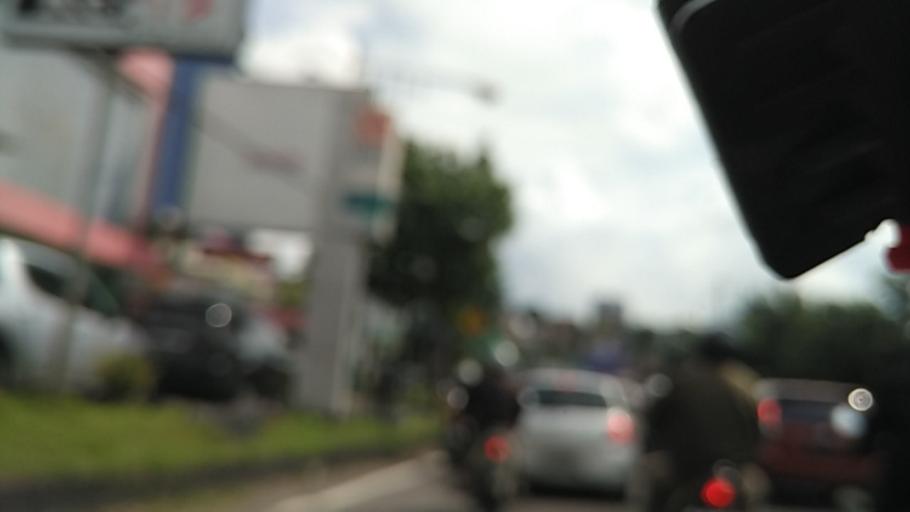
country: ID
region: Central Java
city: Semarang
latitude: -7.0103
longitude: 110.4159
